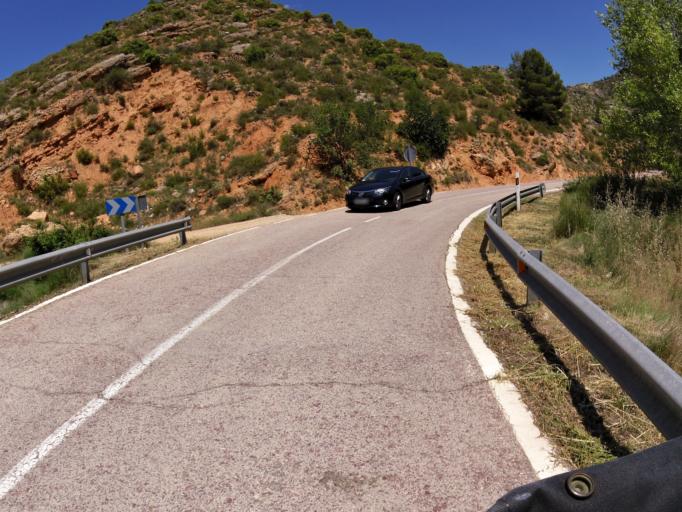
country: ES
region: Valencia
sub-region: Provincia de Valencia
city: Casas Bajas
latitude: 40.0132
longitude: -1.2717
